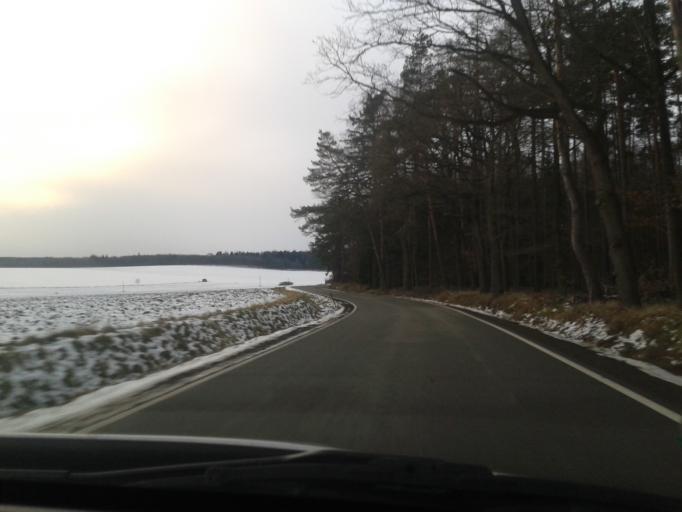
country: CZ
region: Olomoucky
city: Pteni
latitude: 49.5067
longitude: 16.9356
